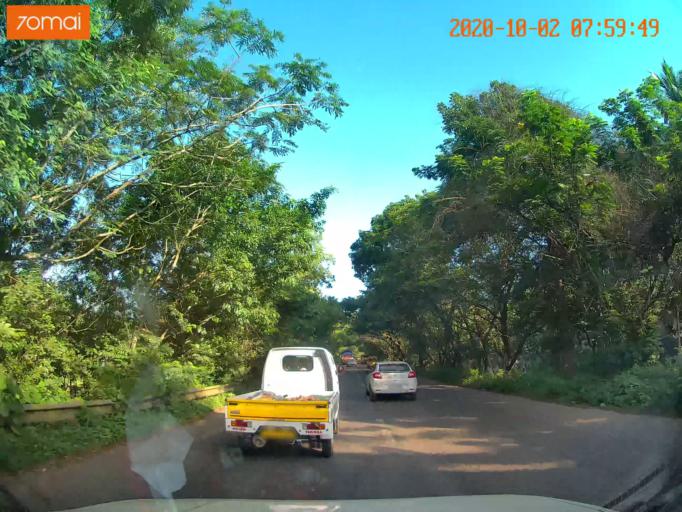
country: IN
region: Kerala
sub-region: Kozhikode
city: Ferokh
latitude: 11.2131
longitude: 75.8597
